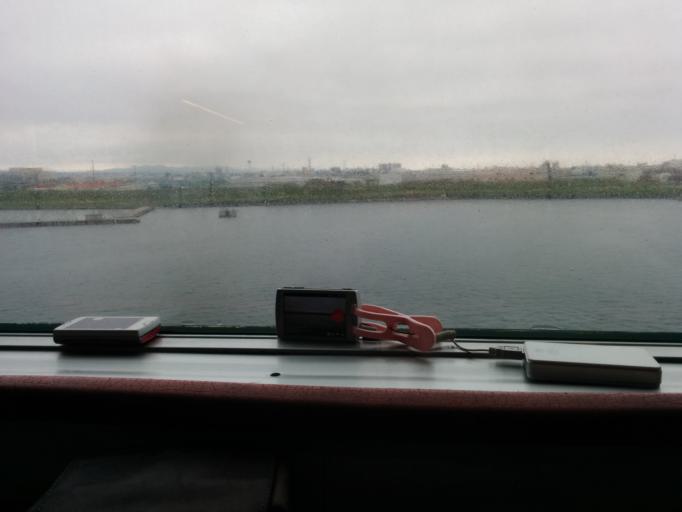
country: JP
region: Hokkaido
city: Hakodate
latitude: 41.8050
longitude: 140.7098
